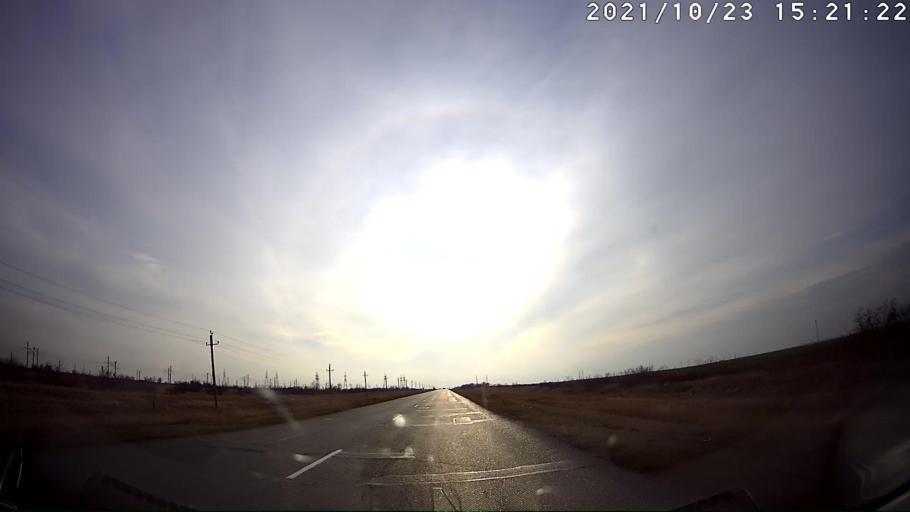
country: RU
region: Volgograd
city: Bereslavka
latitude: 48.3129
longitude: 44.3139
